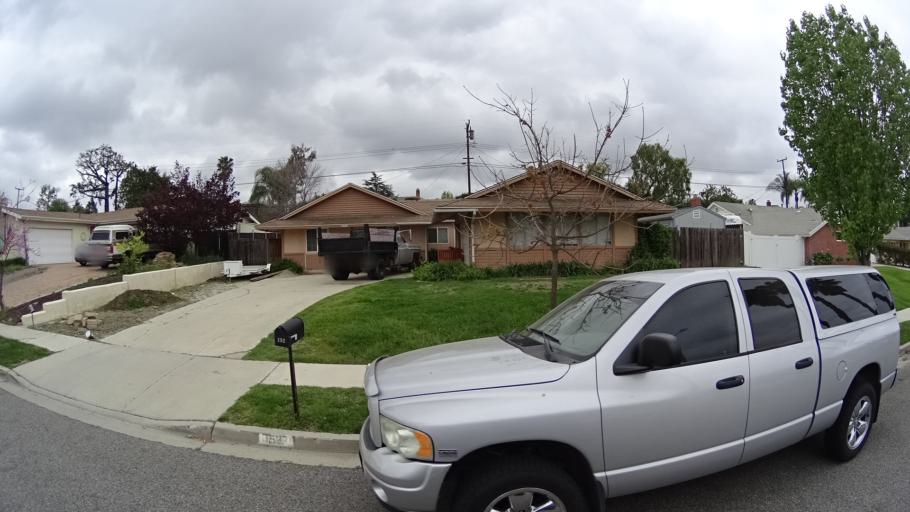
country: US
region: California
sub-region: Ventura County
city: Thousand Oaks
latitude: 34.2144
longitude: -118.8796
